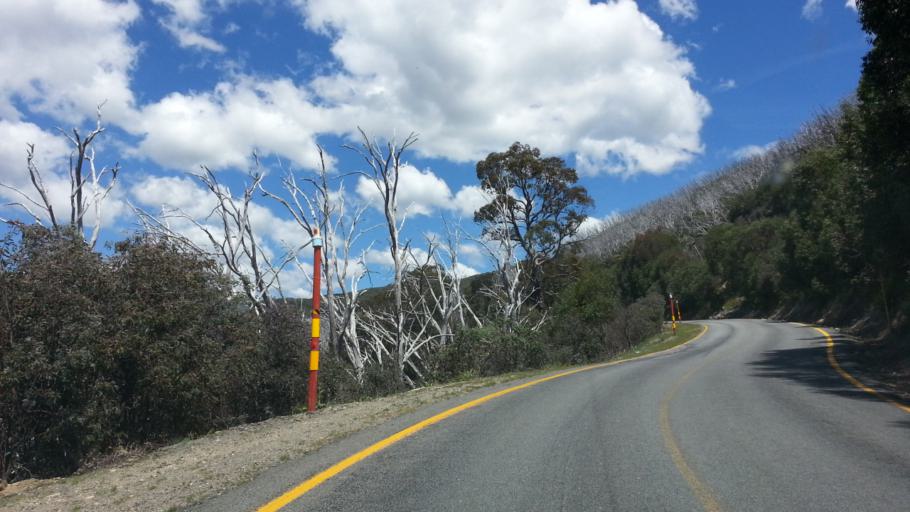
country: AU
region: Victoria
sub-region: Alpine
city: Mount Beauty
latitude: -36.8524
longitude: 147.2719
